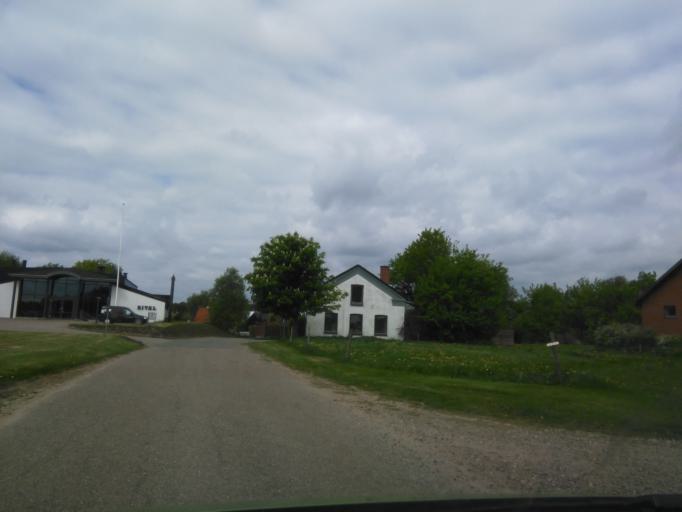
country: DK
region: Central Jutland
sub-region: Skanderborg Kommune
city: Ry
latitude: 56.0687
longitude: 9.8407
